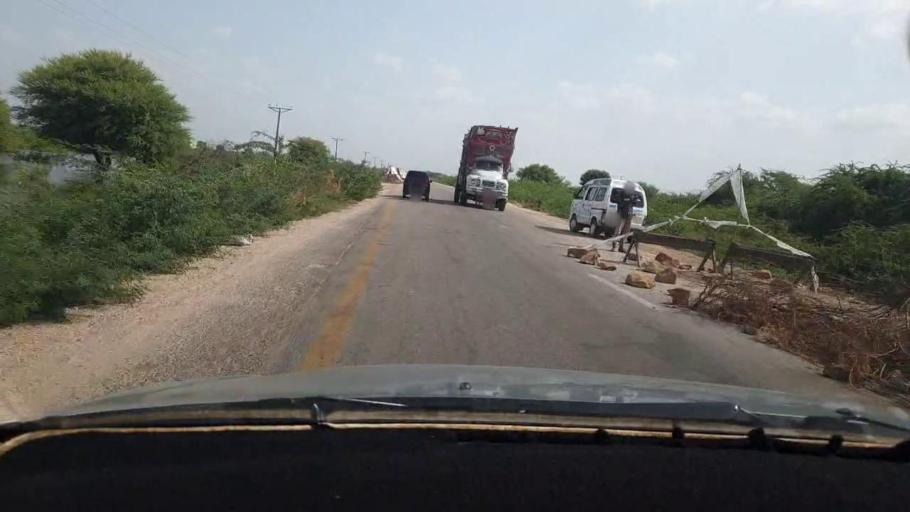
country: PK
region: Sindh
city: Naukot
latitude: 24.9078
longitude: 69.3271
